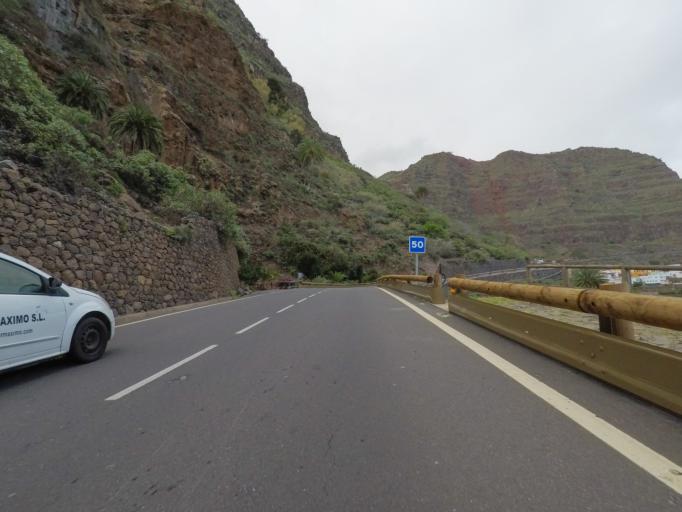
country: ES
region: Canary Islands
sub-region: Provincia de Santa Cruz de Tenerife
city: Agulo
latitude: 28.1852
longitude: -17.1900
